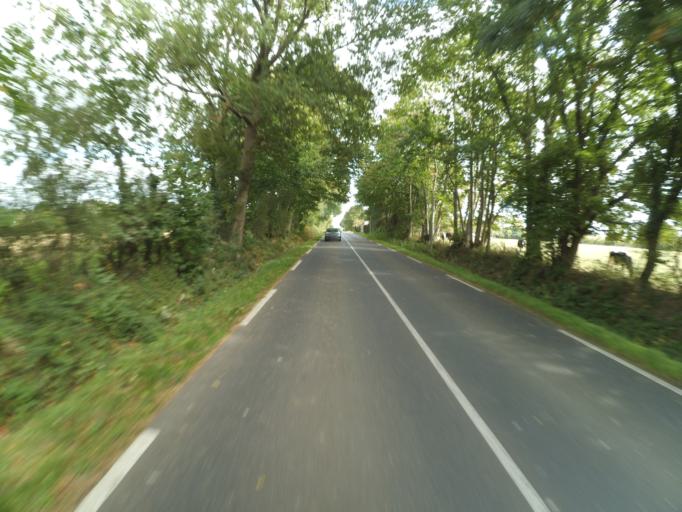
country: FR
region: Pays de la Loire
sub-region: Departement de la Loire-Atlantique
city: Fay-de-Bretagne
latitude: 47.4082
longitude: -1.7499
